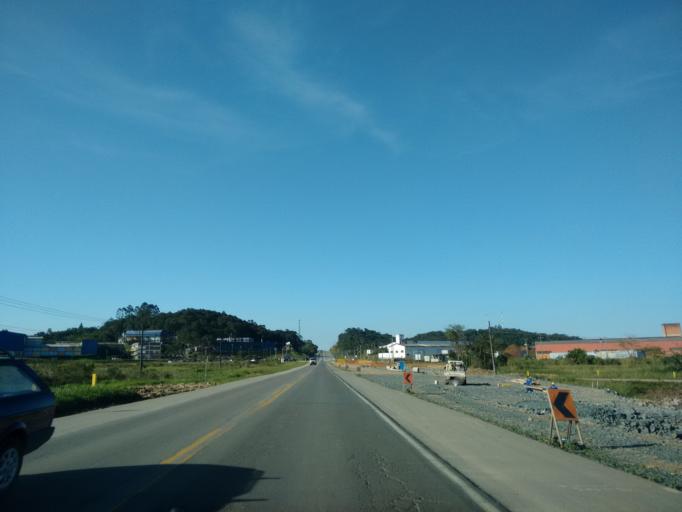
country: BR
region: Santa Catarina
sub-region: Guaramirim
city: Guaramirim
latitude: -26.4616
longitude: -48.9451
